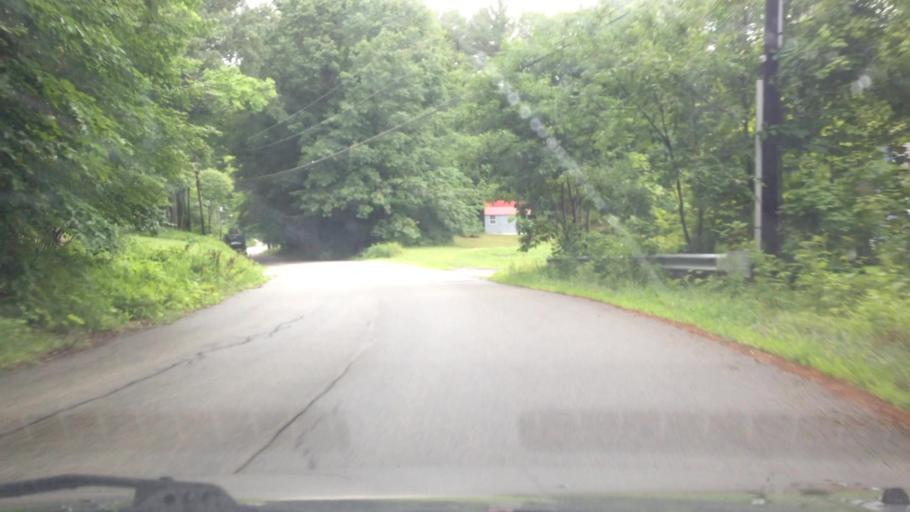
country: US
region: New Hampshire
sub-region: Cheshire County
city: Marlborough
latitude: 42.9014
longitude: -72.1999
